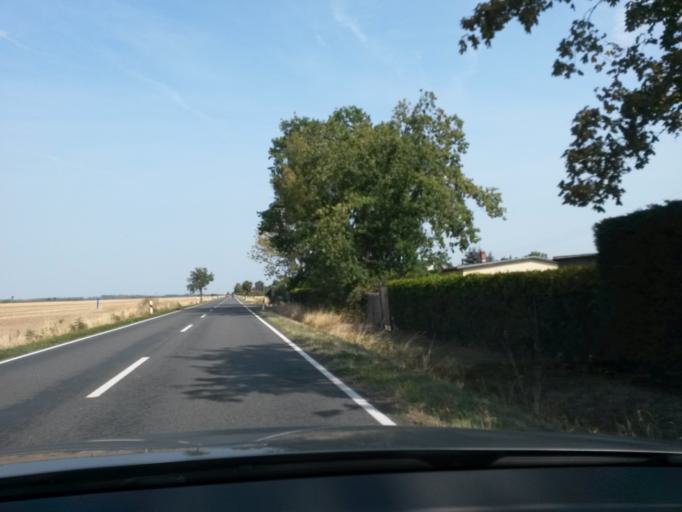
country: DE
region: Saxony-Anhalt
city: Rogatz
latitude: 52.2723
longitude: 11.7769
